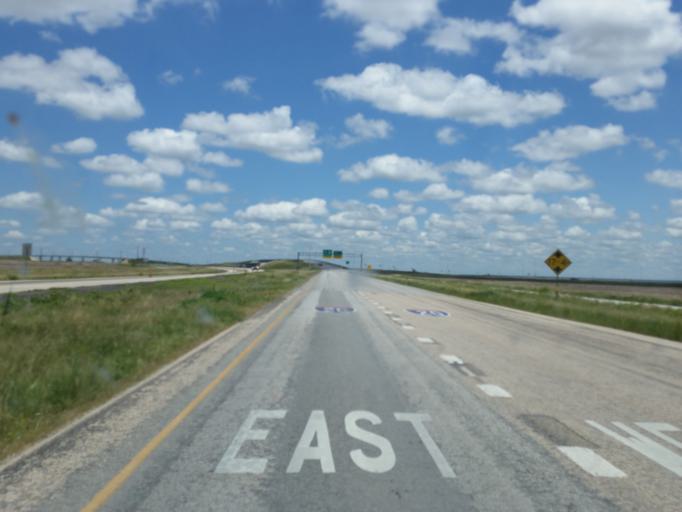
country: US
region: Texas
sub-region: Nolan County
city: Roscoe
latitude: 32.4471
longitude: -100.5128
